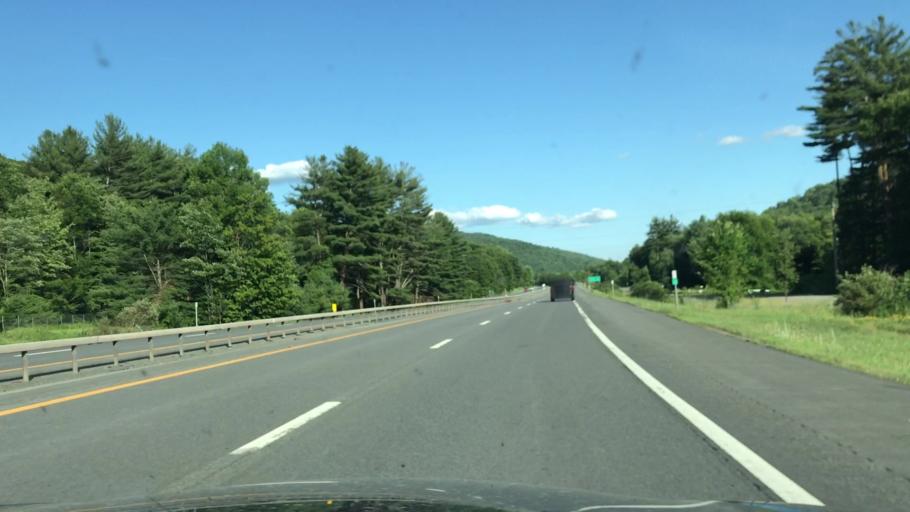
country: US
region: New York
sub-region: Delaware County
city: Hancock
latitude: 41.9863
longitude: -75.1162
